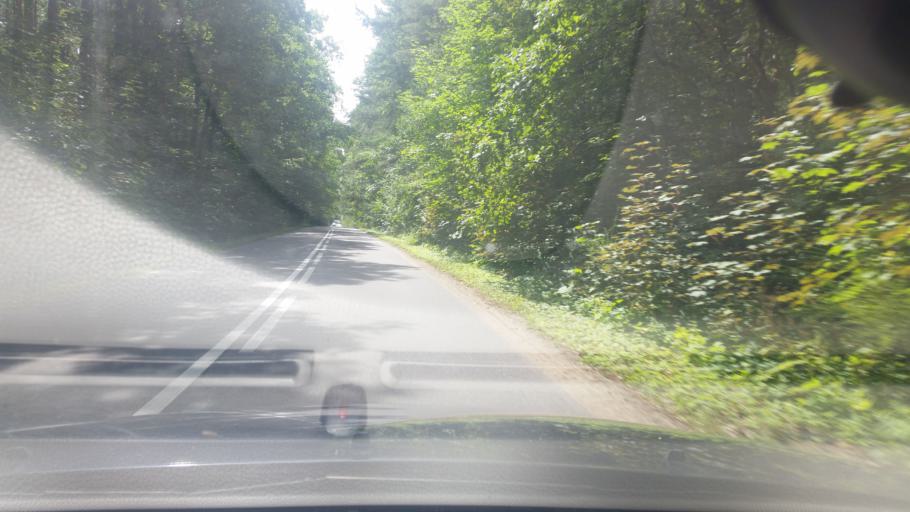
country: PL
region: Pomeranian Voivodeship
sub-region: Powiat wejherowski
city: Choczewo
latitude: 54.7553
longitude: 17.7480
